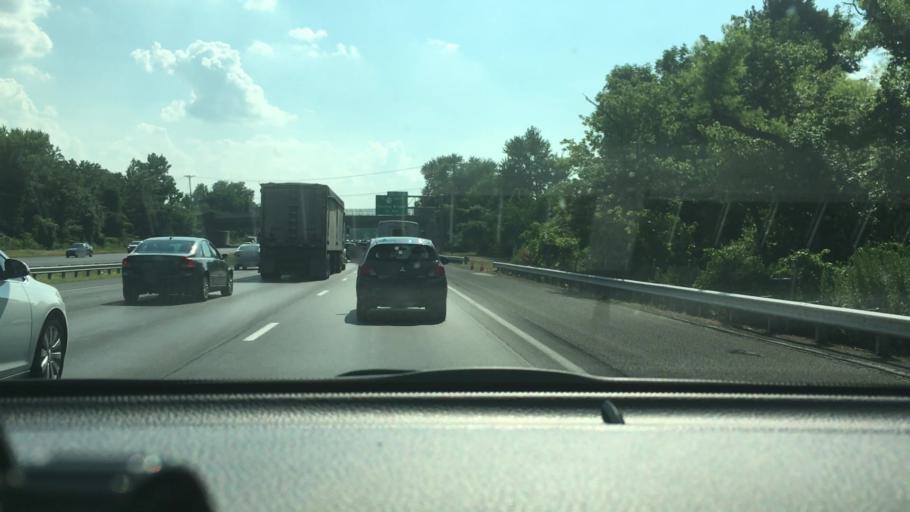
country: US
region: New Jersey
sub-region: Burlington County
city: Ramblewood
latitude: 39.9406
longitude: -74.9527
